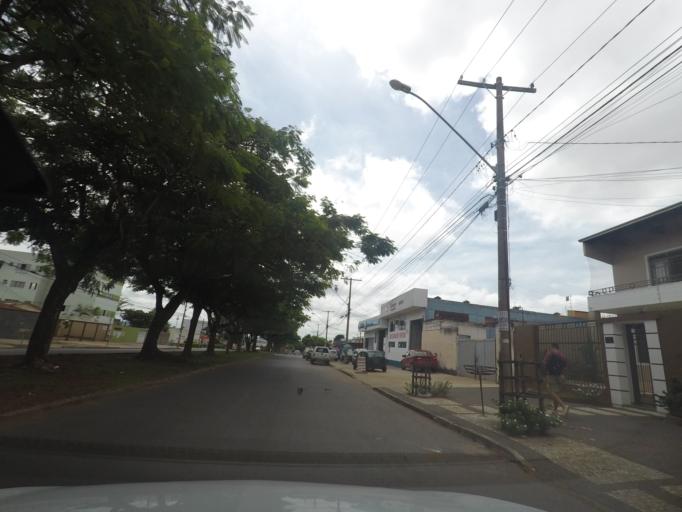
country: BR
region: Goias
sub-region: Goiania
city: Goiania
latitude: -16.6741
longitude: -49.2338
